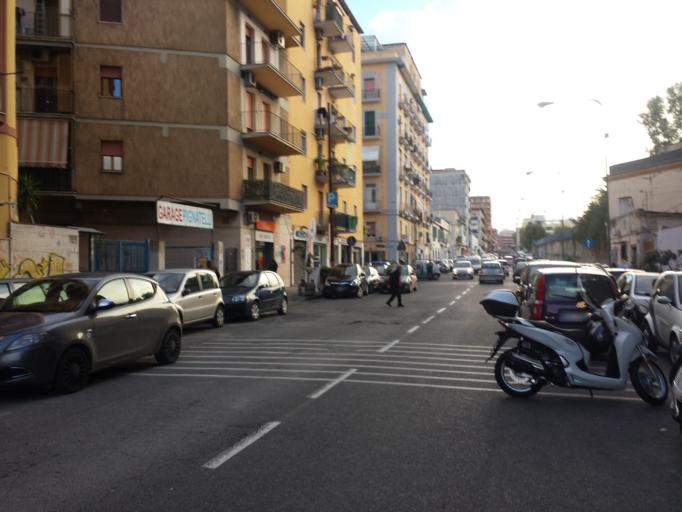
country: IT
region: Campania
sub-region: Provincia di Napoli
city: Napoli
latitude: 40.8592
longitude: 14.2735
